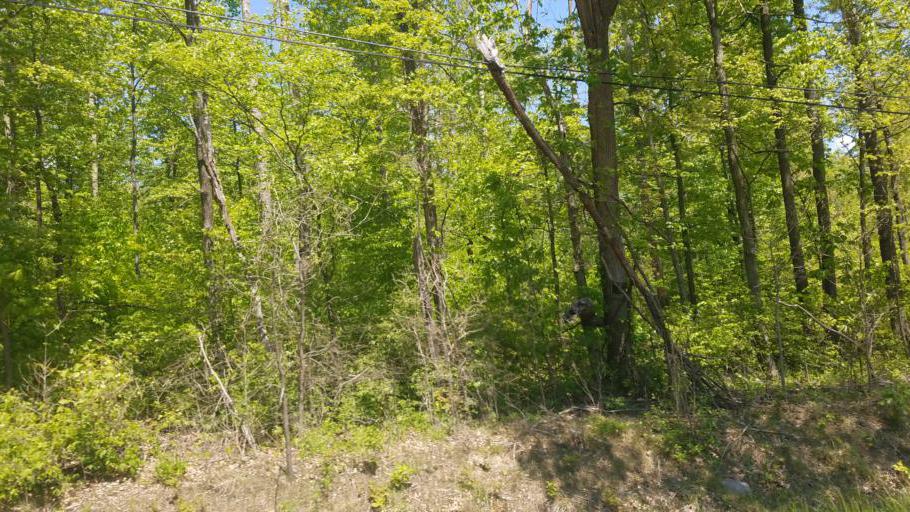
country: US
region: Ohio
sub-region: Muskingum County
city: Frazeysburg
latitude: 40.2247
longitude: -82.2650
